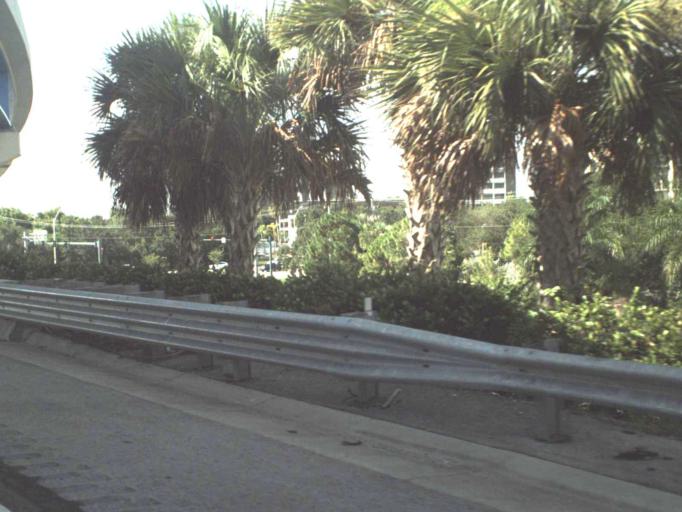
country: US
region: Florida
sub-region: Palm Beach County
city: North Palm Beach
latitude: 26.8405
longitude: -80.1028
